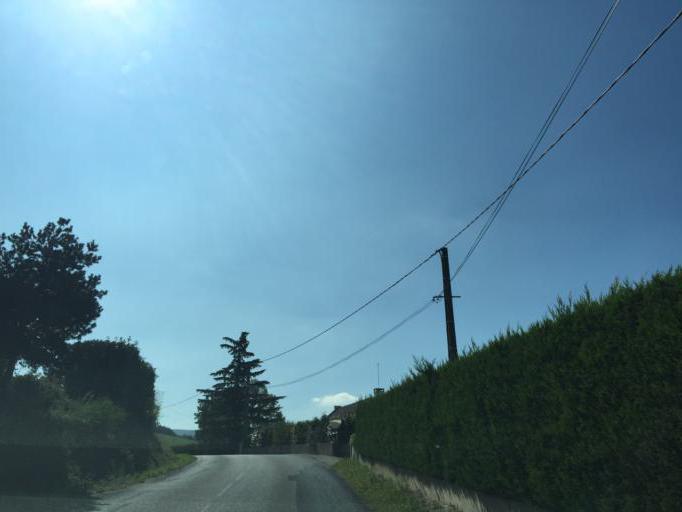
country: FR
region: Rhone-Alpes
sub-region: Departement de la Loire
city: Saint-Paul-en-Jarez
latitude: 45.4717
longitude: 4.5614
